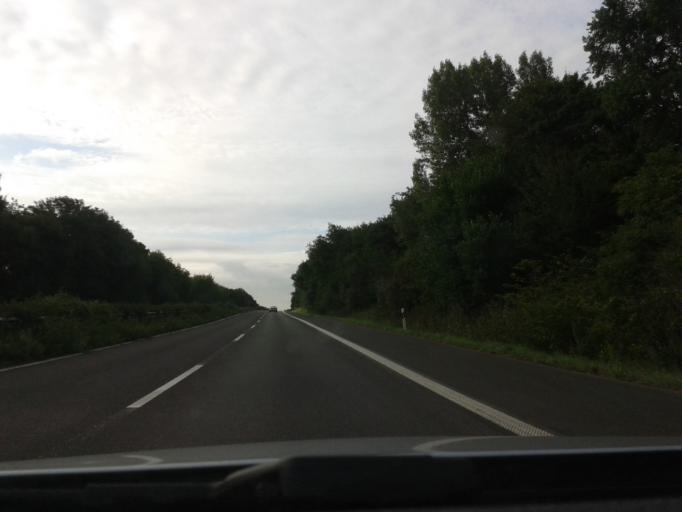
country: DE
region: North Rhine-Westphalia
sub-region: Regierungsbezirk Dusseldorf
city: Moers
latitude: 51.4249
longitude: 6.6768
